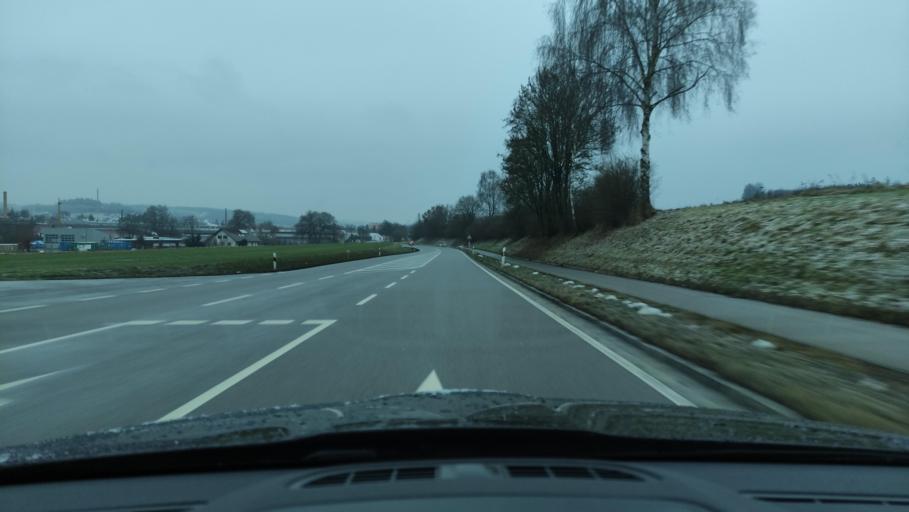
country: DE
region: Bavaria
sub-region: Swabia
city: Krumbach
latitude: 48.2579
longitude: 10.3522
